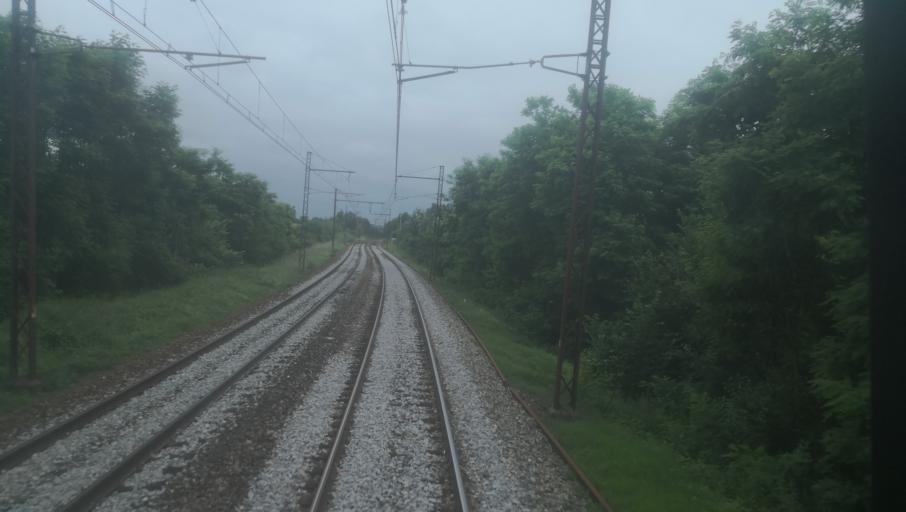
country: FR
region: Centre
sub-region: Departement de l'Indre
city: Le Pechereau
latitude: 46.5328
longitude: 1.5347
